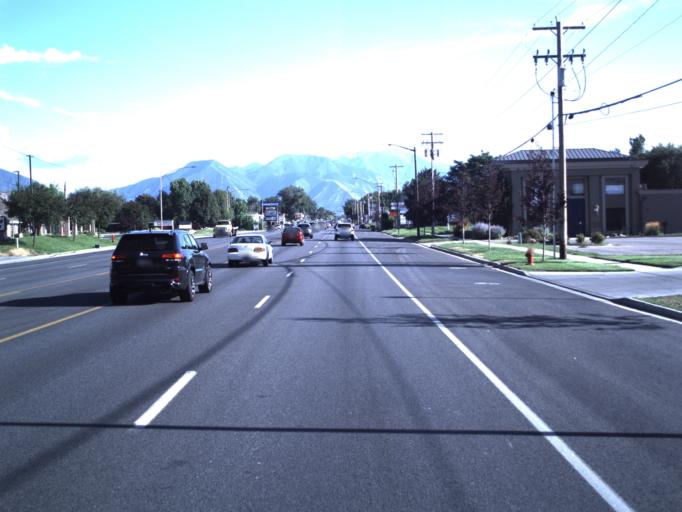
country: US
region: Utah
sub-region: Utah County
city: Springville
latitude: 40.1784
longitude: -111.6107
